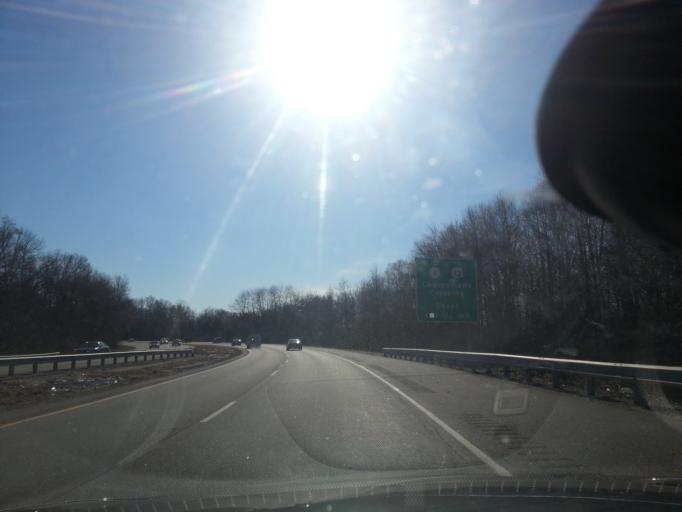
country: US
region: Delaware
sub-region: New Castle County
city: Bear
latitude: 39.6591
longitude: -75.6621
